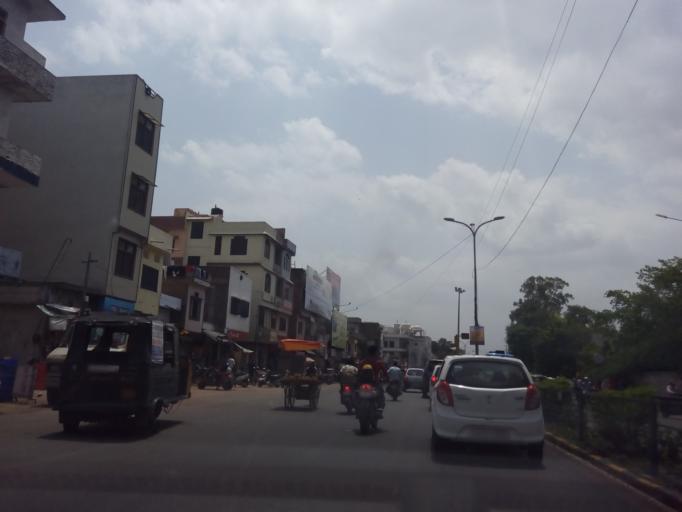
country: IN
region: Rajasthan
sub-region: Udaipur
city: Udaipur
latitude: 24.5795
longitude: 73.7102
